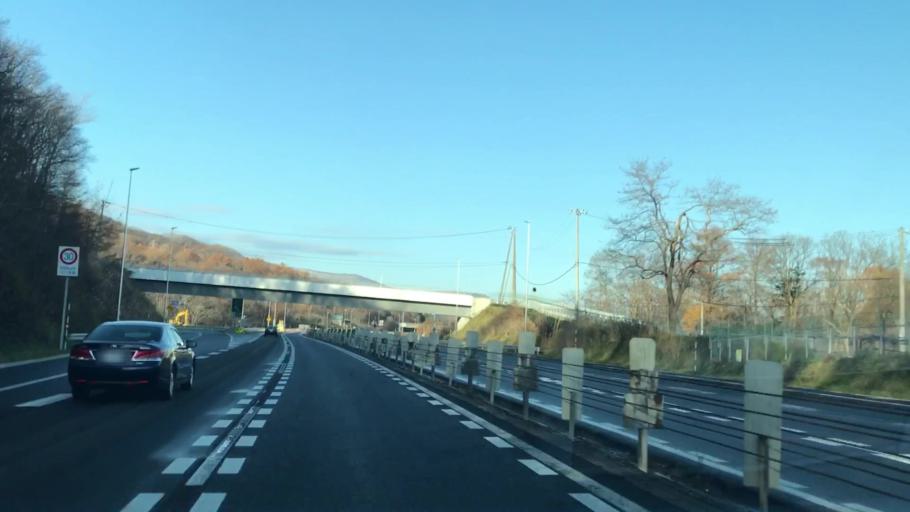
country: JP
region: Hokkaido
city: Sapporo
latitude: 43.1328
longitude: 141.1786
